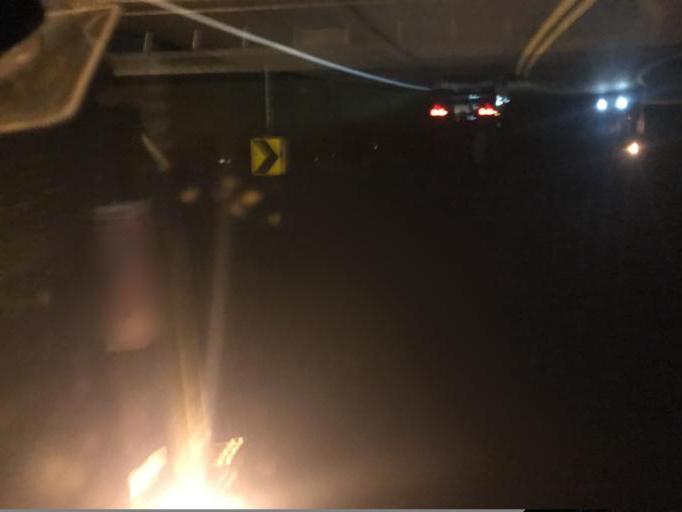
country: TW
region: Taiwan
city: Daxi
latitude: 24.8335
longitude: 121.2017
